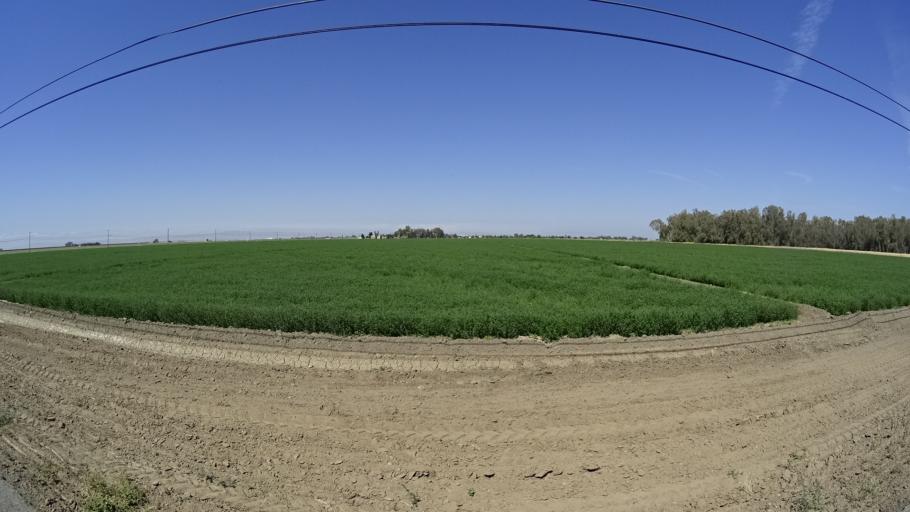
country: US
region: California
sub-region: Kings County
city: Stratford
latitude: 36.1913
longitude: -119.7977
